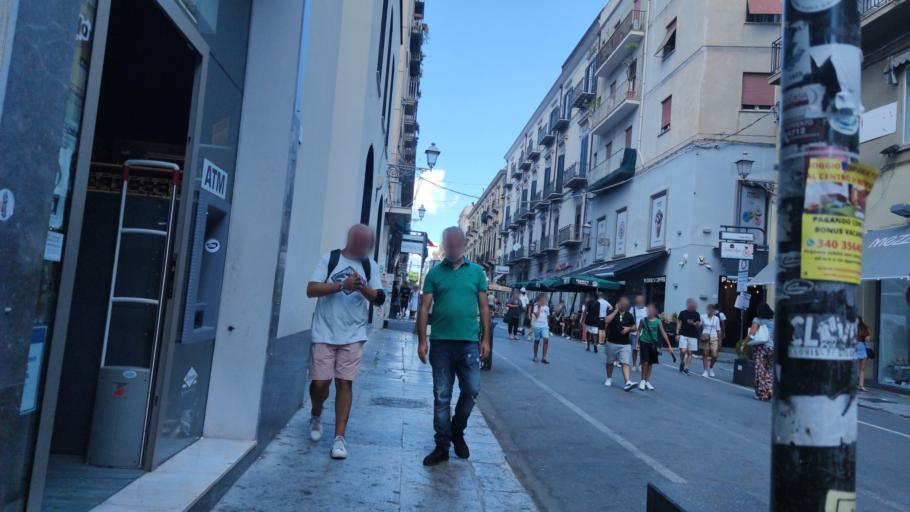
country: IT
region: Sicily
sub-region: Palermo
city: Palermo
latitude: 38.1182
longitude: 13.3598
